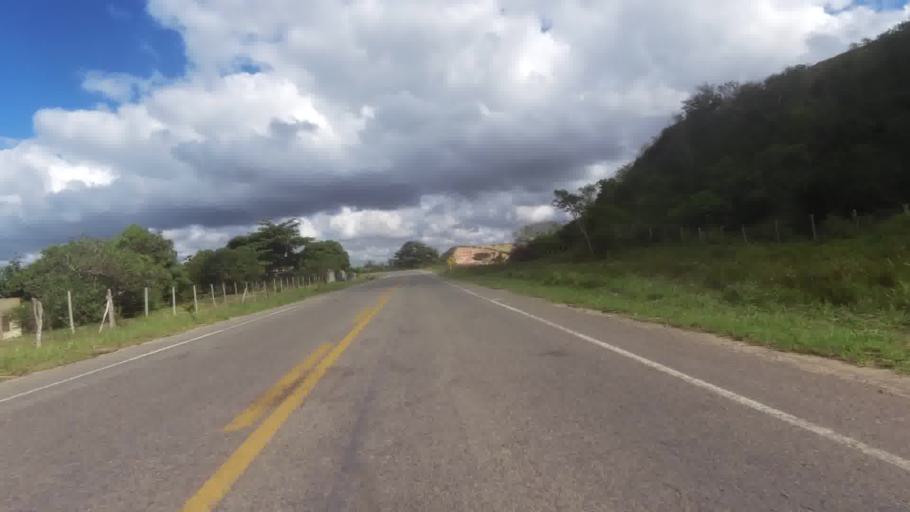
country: BR
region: Espirito Santo
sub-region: Marataizes
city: Marataizes
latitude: -21.1851
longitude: -40.9298
